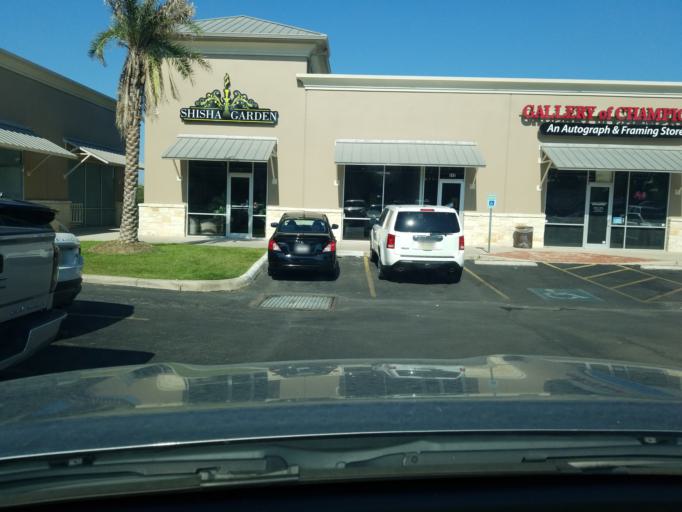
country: US
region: Texas
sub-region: Bexar County
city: Hollywood Park
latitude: 29.6243
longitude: -98.4960
